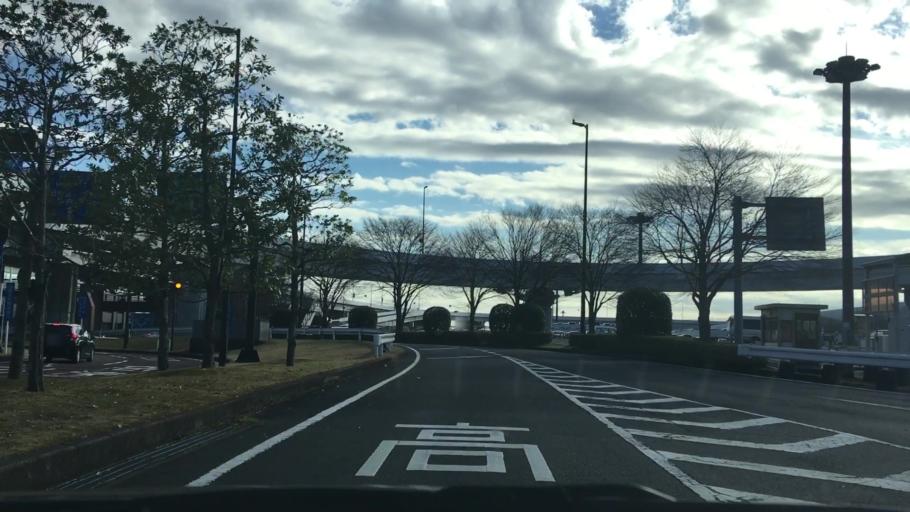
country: JP
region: Chiba
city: Narita
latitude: 35.7715
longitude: 140.3882
